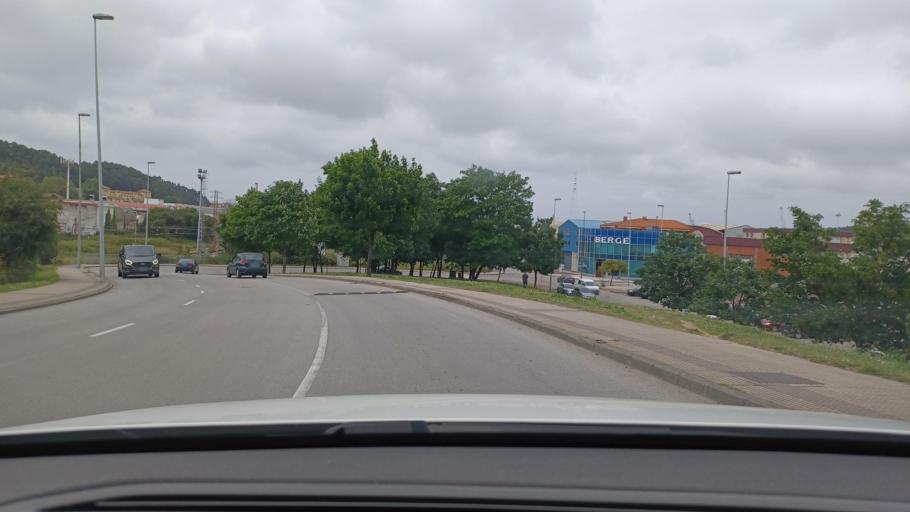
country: ES
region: Asturias
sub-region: Province of Asturias
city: Aviles
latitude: 43.5658
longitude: -5.9253
